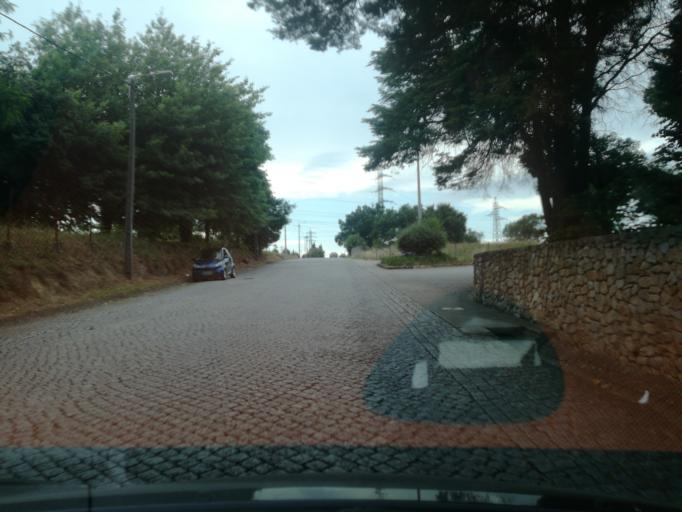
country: PT
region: Porto
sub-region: Maia
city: Leca do Bailio
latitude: 41.2281
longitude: -8.6055
